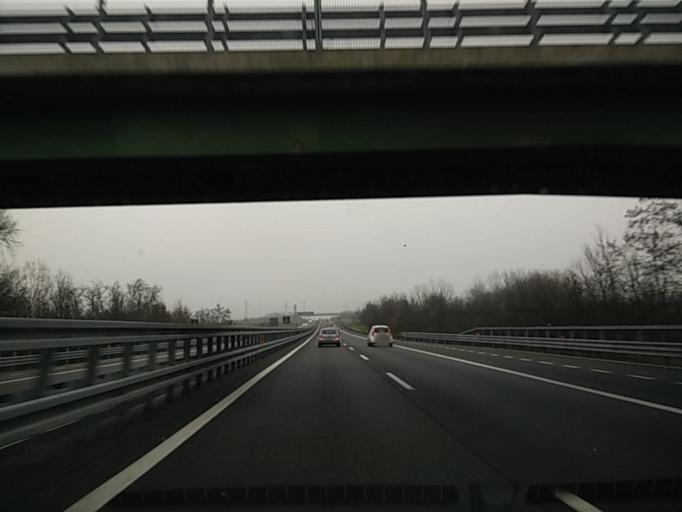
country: IT
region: Piedmont
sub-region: Provincia di Alessandria
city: Felizzano
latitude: 44.9122
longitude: 8.4208
